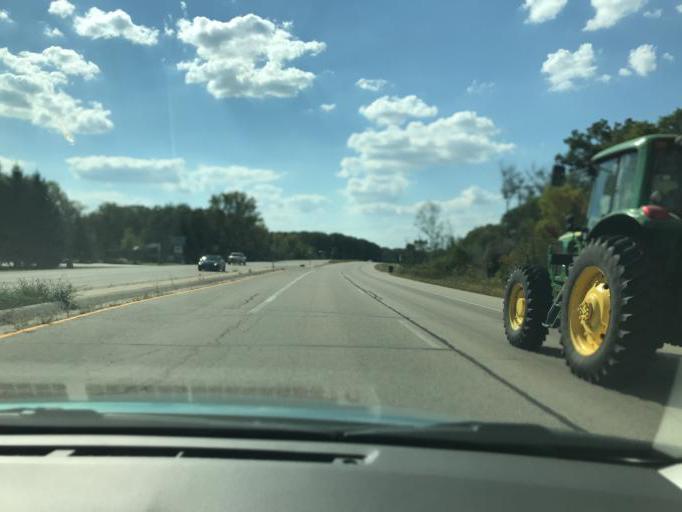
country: US
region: Wisconsin
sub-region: Walworth County
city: Como
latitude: 42.5835
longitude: -88.4972
